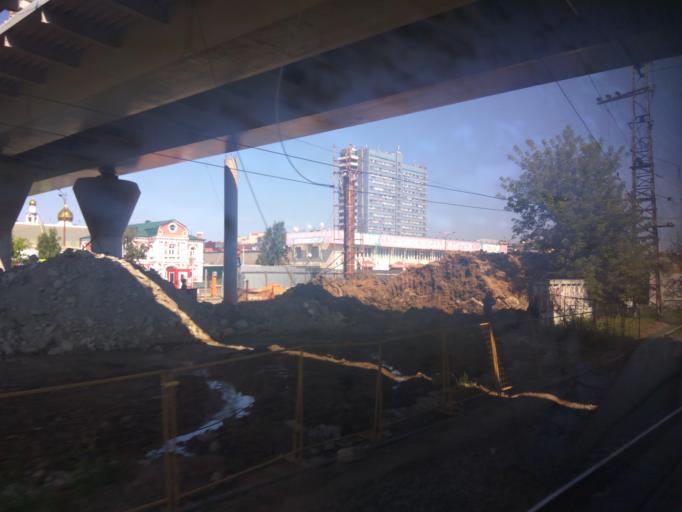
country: RU
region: Moskovskaya
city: Odintsovo
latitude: 55.6698
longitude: 37.2771
